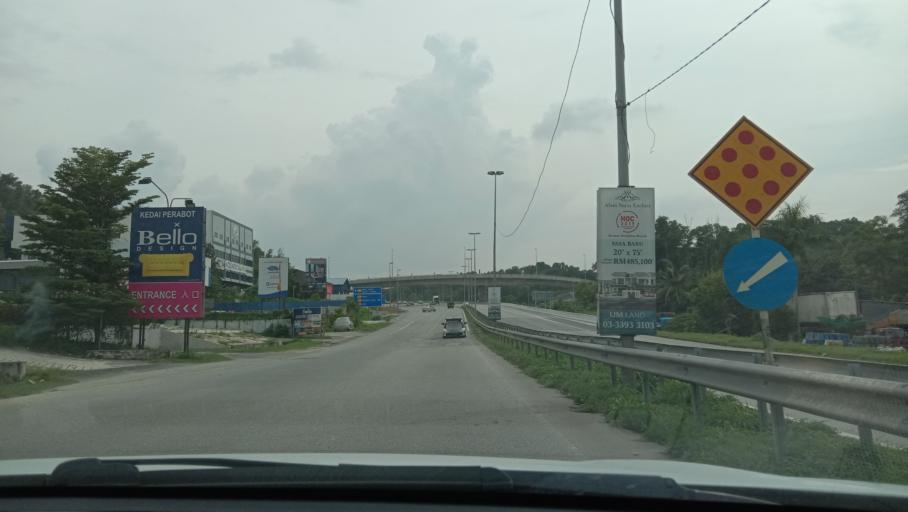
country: MY
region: Selangor
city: Kampung Baru Subang
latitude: 3.1308
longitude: 101.5259
